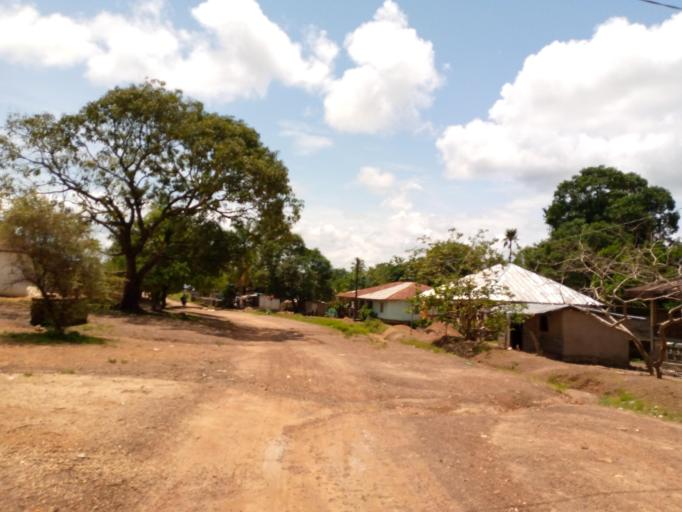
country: SL
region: Northern Province
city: Magburaka
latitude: 8.7145
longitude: -11.9595
